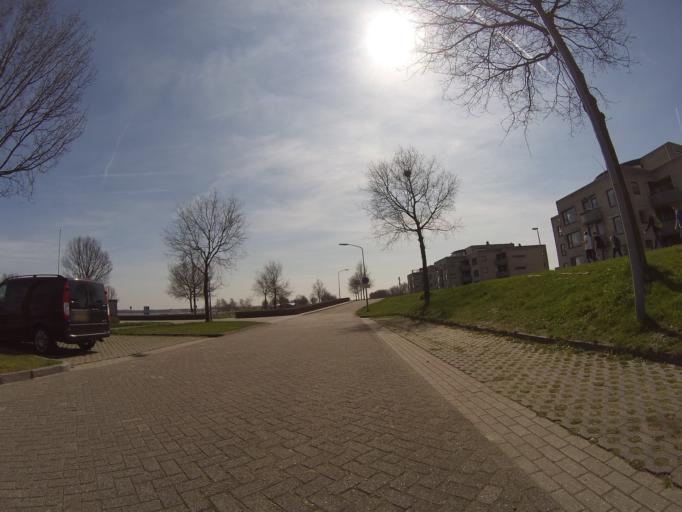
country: NL
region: Flevoland
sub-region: Gemeente Zeewolde
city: Zeewolde
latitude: 52.3283
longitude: 5.5464
